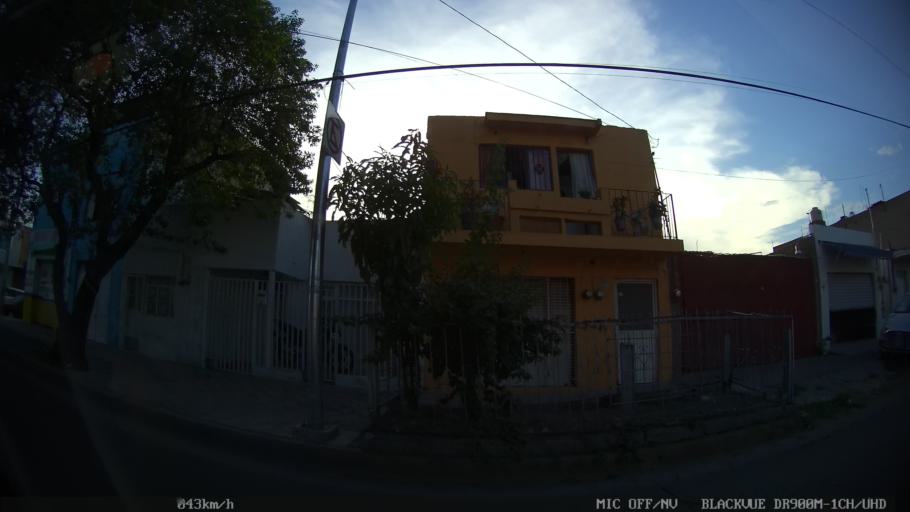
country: MX
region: Jalisco
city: Tlaquepaque
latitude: 20.6840
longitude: -103.3099
